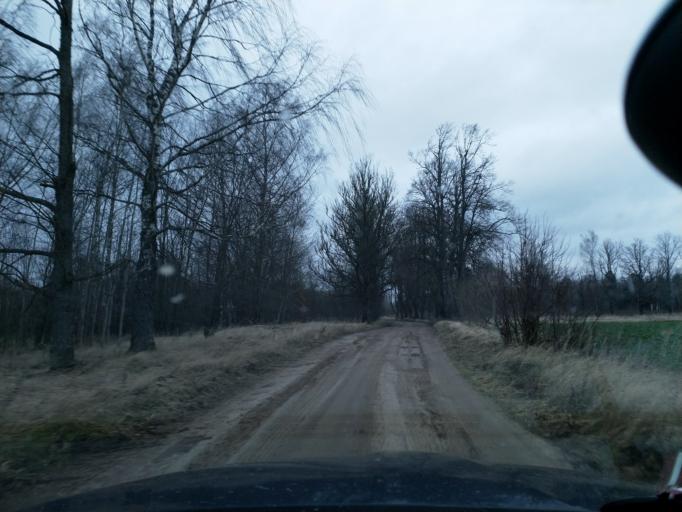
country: LV
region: Saldus Rajons
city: Saldus
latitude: 56.8945
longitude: 22.3204
